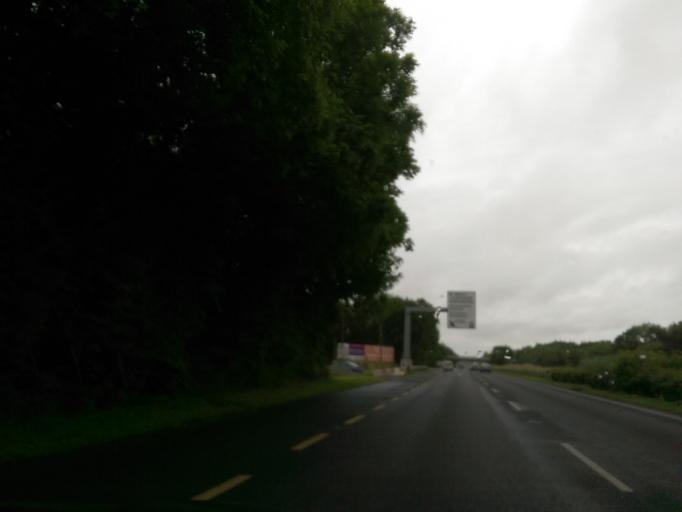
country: IE
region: Munster
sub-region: An Clar
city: Sixmilebridge
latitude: 52.6892
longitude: -8.7439
